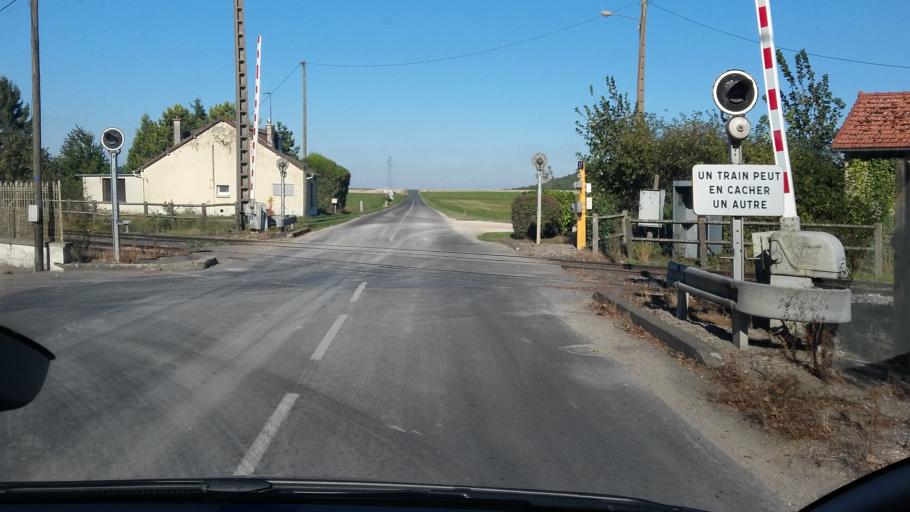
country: FR
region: Champagne-Ardenne
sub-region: Departement de la Marne
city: Vertus
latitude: 48.8512
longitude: 3.9705
